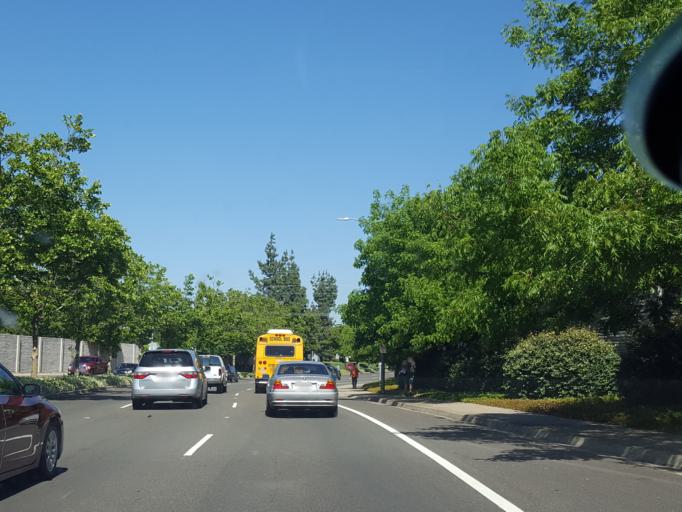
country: US
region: California
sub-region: Sacramento County
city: Rancho Cordova
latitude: 38.5737
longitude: -121.3000
